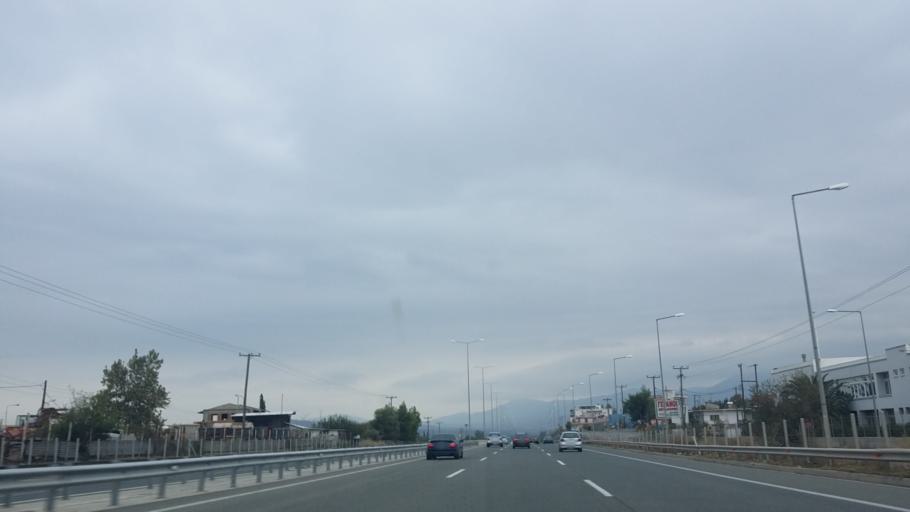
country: GR
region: Central Greece
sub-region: Nomos Voiotias
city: Oinofyta
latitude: 38.3139
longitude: 23.6334
